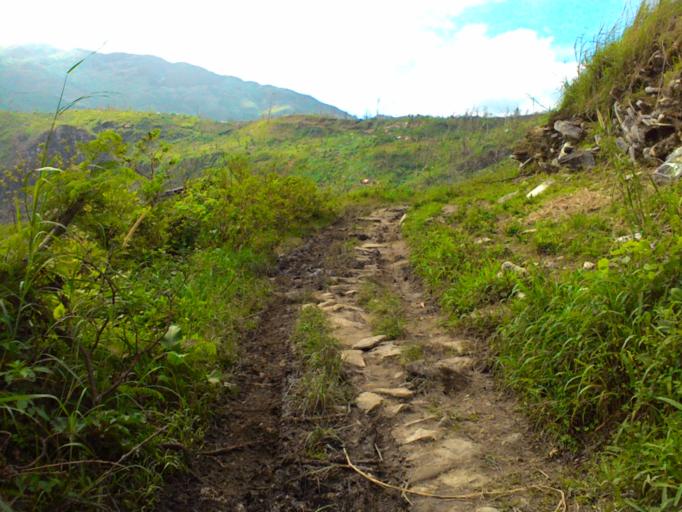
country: HT
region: Grandans
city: Moron
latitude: 18.4616
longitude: -74.1144
